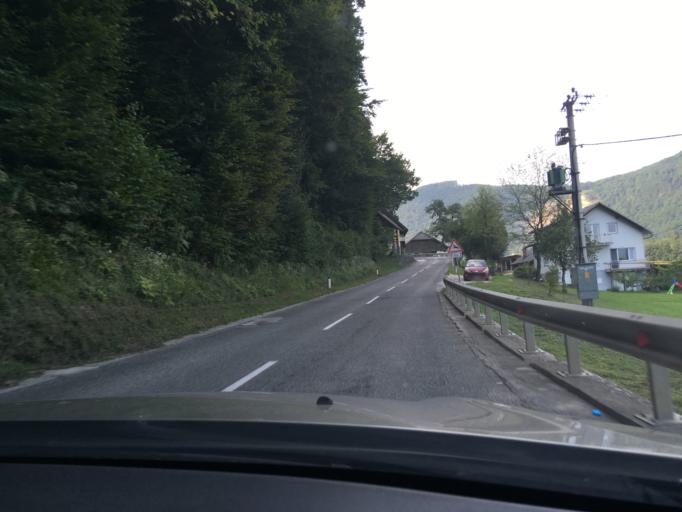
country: SI
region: Dolenjske Toplice
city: Dolenjske Toplice
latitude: 45.7682
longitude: 15.0248
